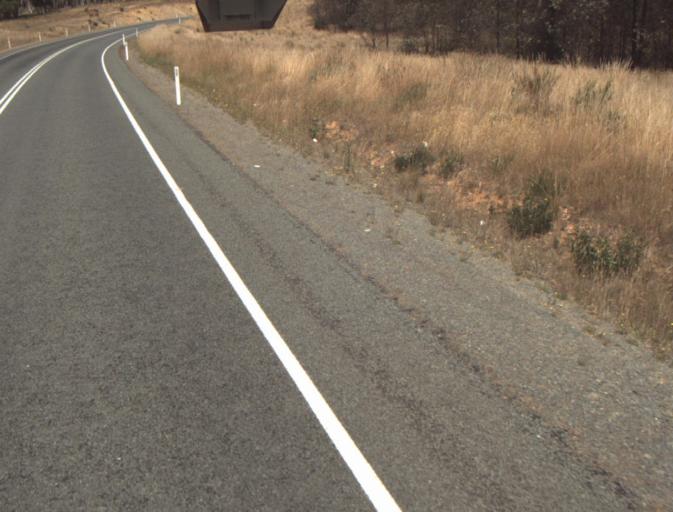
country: AU
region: Tasmania
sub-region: Launceston
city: Newstead
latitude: -41.3381
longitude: 147.3474
